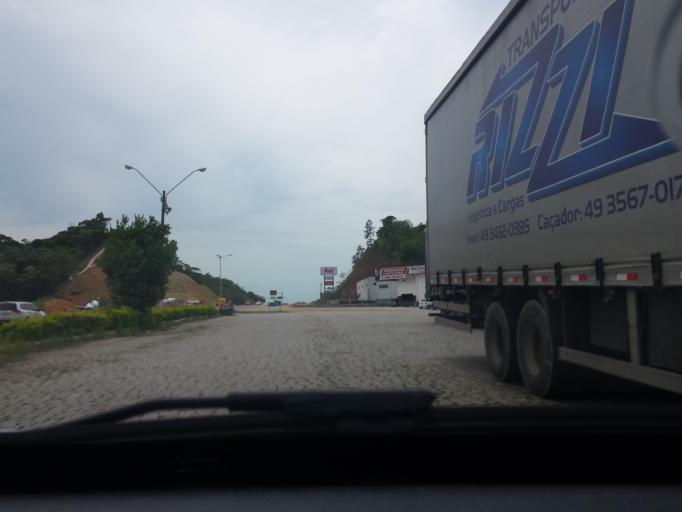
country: BR
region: Santa Catarina
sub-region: Gaspar
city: Gaspar
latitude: -26.9146
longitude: -48.9706
